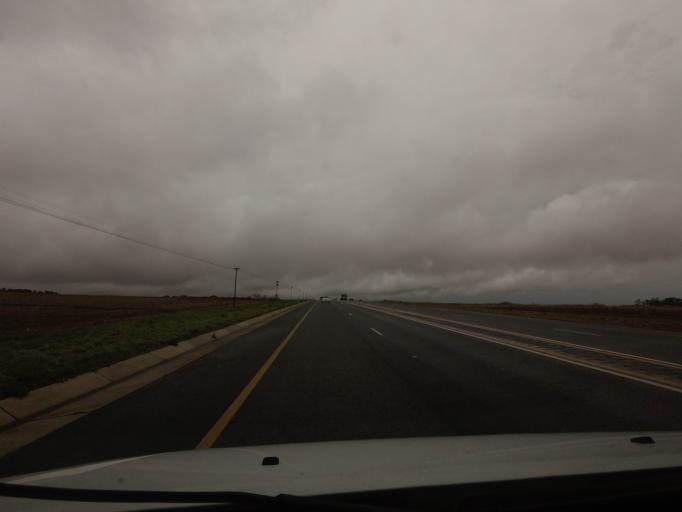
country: ZA
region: Mpumalanga
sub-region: Nkangala District Municipality
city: Belfast
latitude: -25.7865
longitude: 29.9278
